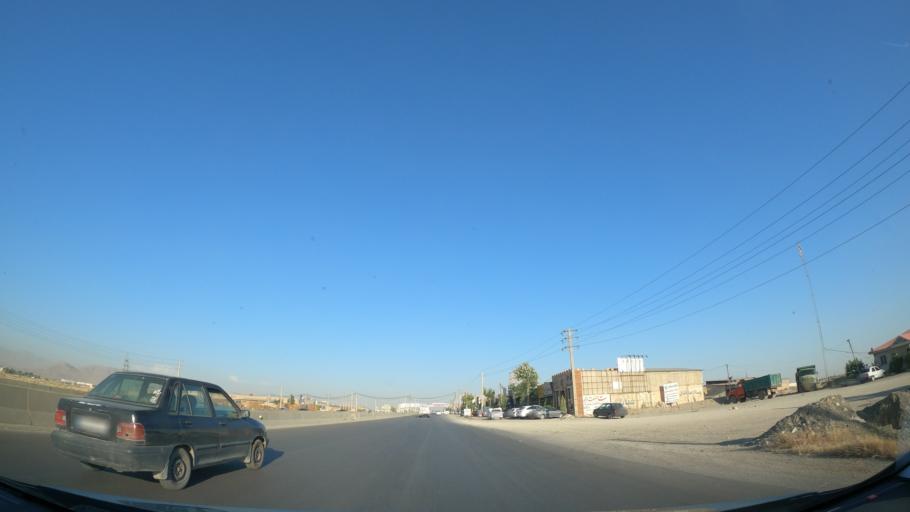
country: IR
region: Alborz
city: Hashtgerd
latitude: 35.9192
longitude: 50.7503
